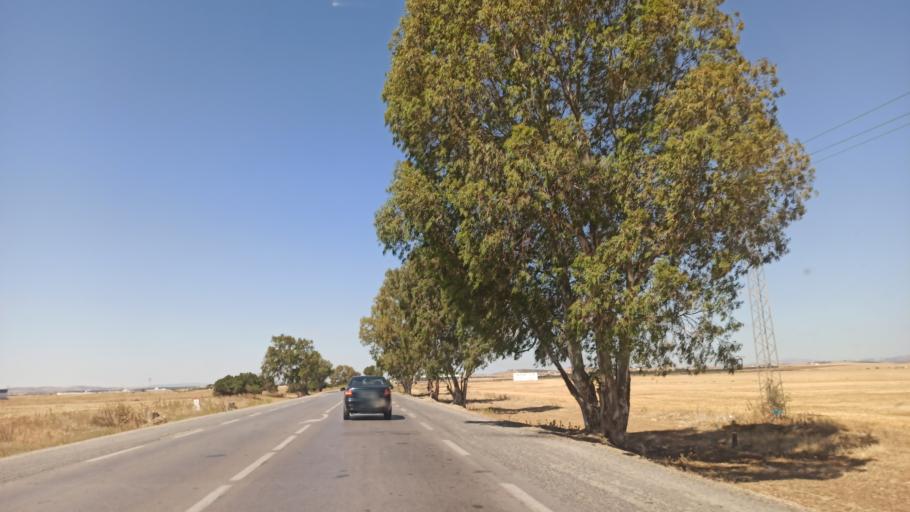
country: TN
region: Tunis
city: Oued Lill
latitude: 36.7427
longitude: 9.9587
